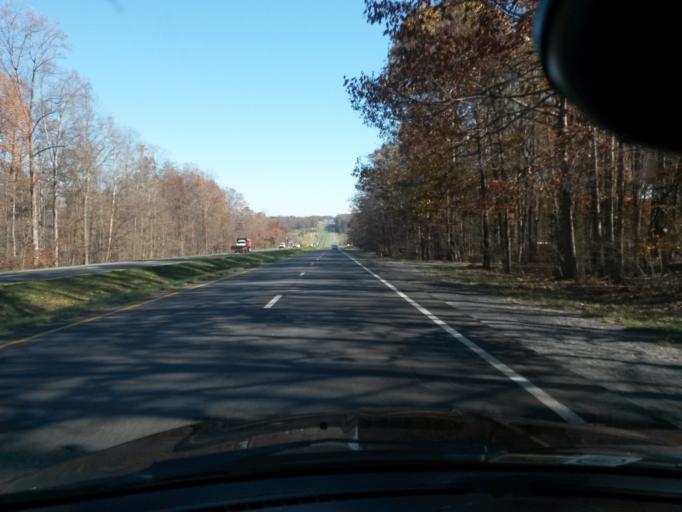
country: US
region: Virginia
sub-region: Bedford County
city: Forest
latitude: 37.3014
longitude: -79.3331
